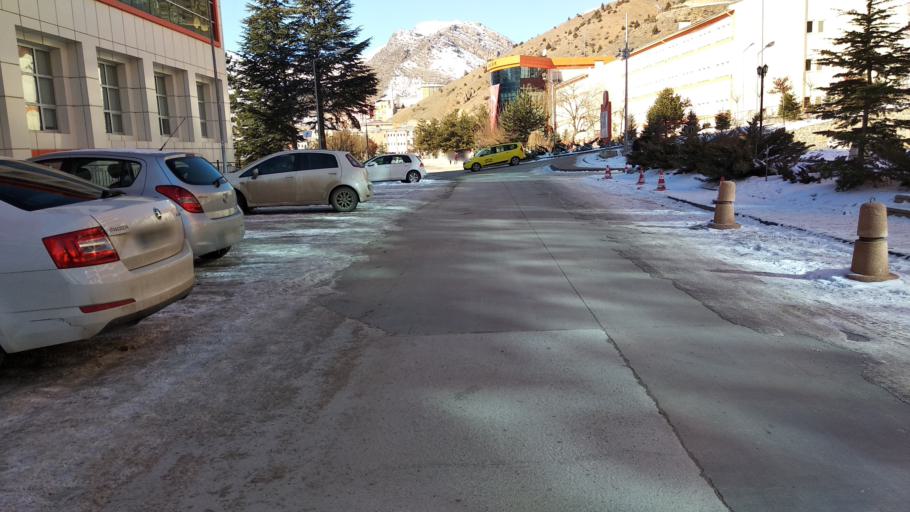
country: TR
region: Gumushane
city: Gumushkhane
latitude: 40.4361
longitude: 39.5171
